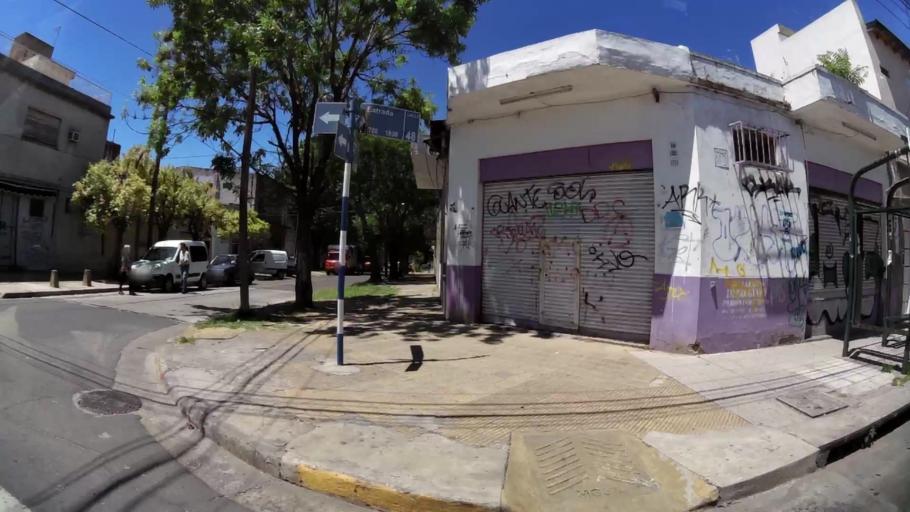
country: AR
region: Buenos Aires
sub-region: Partido de General San Martin
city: General San Martin
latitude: -34.5673
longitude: -58.5192
